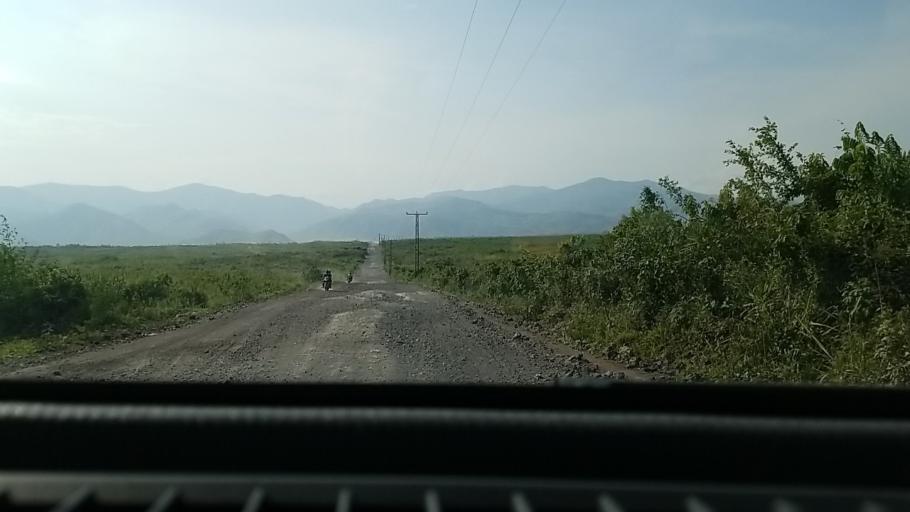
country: CD
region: Nord Kivu
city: Sake
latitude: -1.5860
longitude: 29.0885
